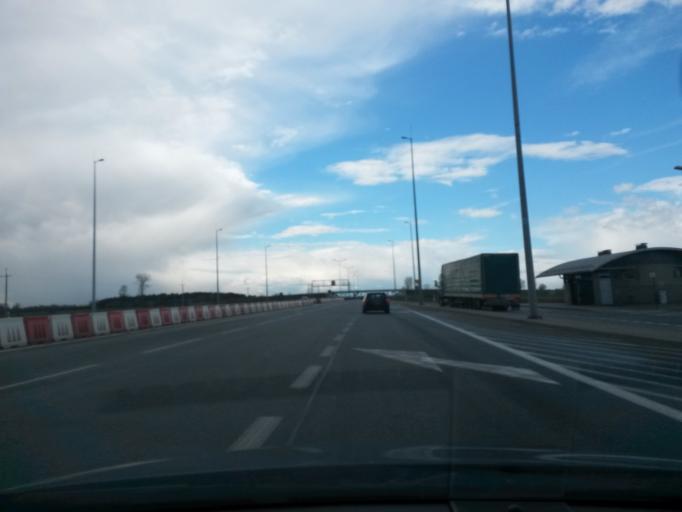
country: PL
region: Greater Poland Voivodeship
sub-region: Powiat slupecki
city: Ladek
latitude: 52.2226
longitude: 17.9490
